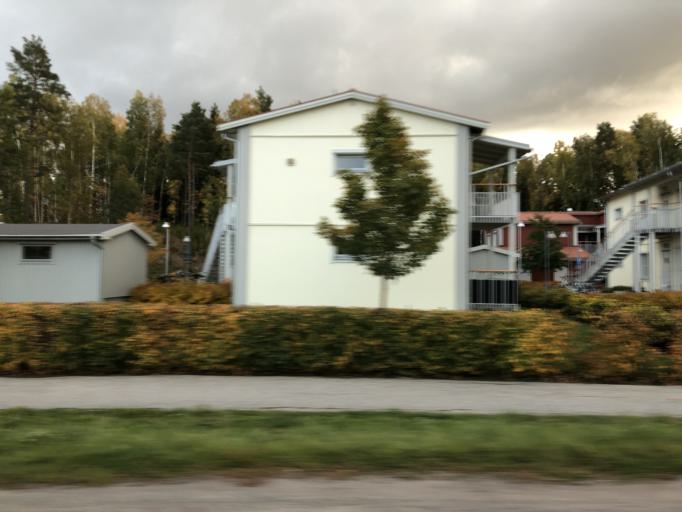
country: SE
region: Stockholm
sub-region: Jarfalla Kommun
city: Jakobsberg
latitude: 59.4224
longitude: 17.8031
